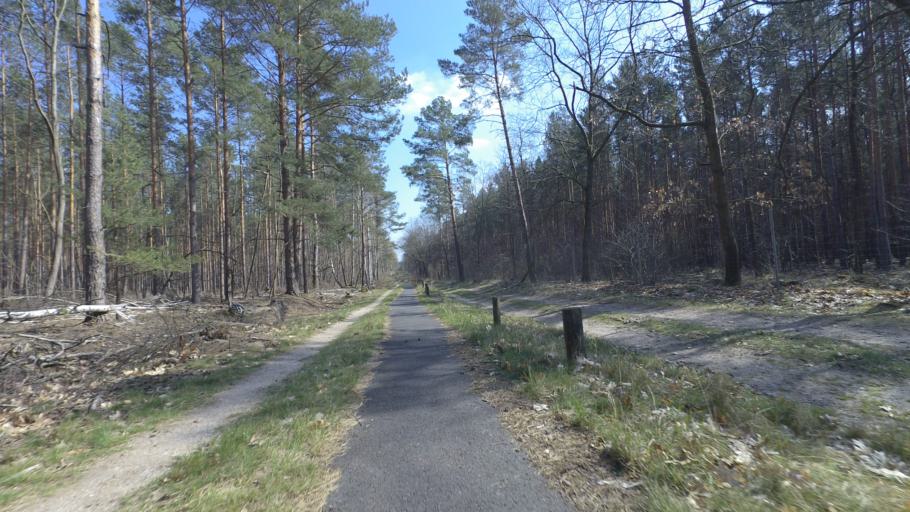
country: DE
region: Brandenburg
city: Mittenwalde
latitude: 52.1862
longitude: 13.5404
